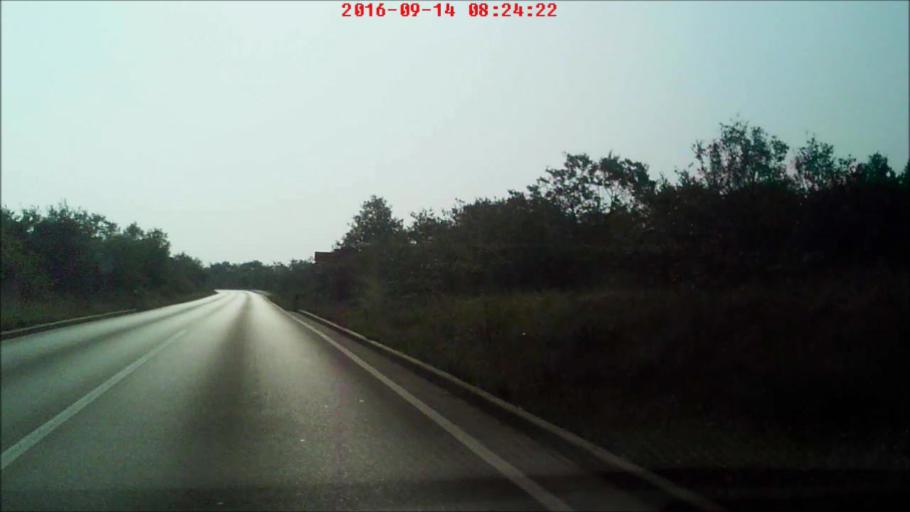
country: HR
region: Zadarska
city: Vrsi
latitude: 44.2070
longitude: 15.2432
